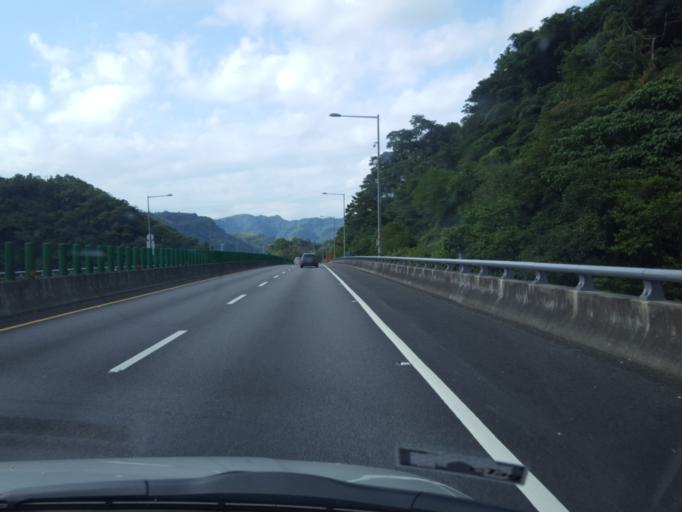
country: TW
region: Taipei
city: Taipei
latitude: 24.9859
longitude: 121.6602
